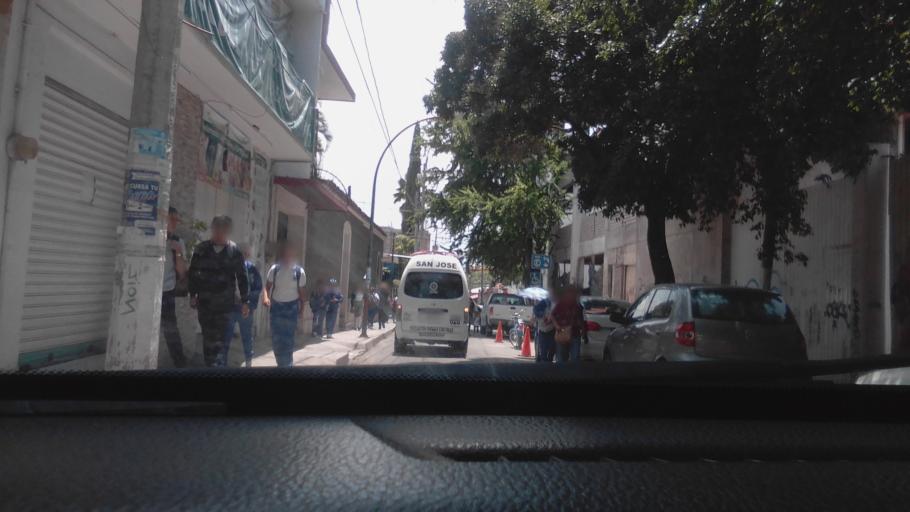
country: MX
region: Guerrero
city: Chilpancingo de los Bravos
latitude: 17.5569
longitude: -99.5035
